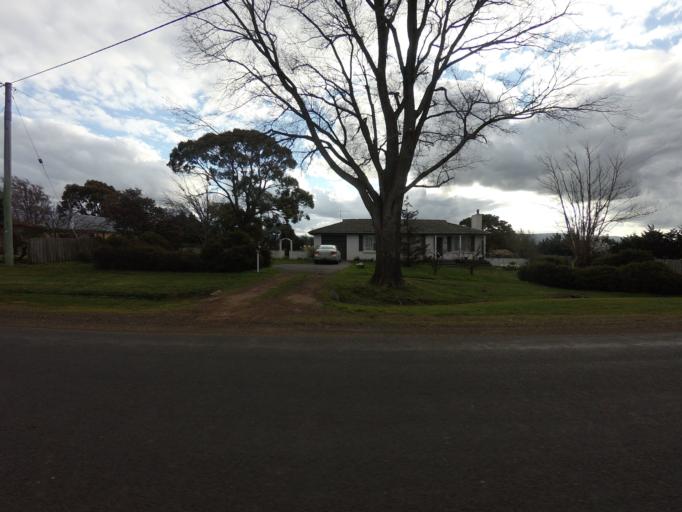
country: AU
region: Tasmania
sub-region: Northern Midlands
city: Evandale
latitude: -42.0262
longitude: 147.4933
